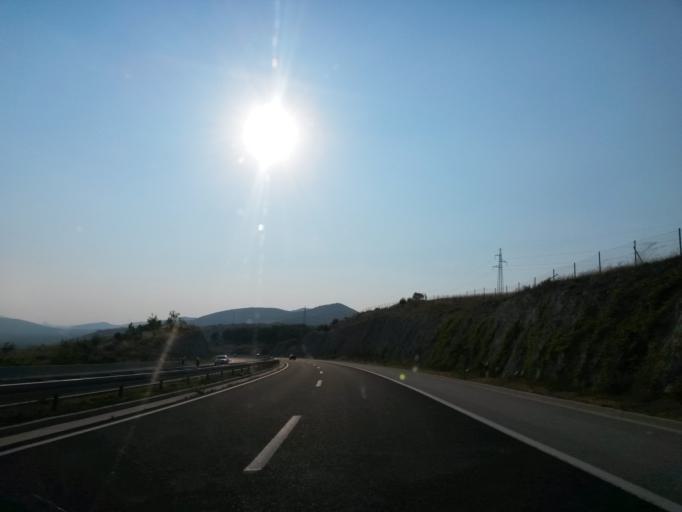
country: HR
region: Splitsko-Dalmatinska
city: Dugopolje
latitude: 43.6028
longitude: 16.6194
